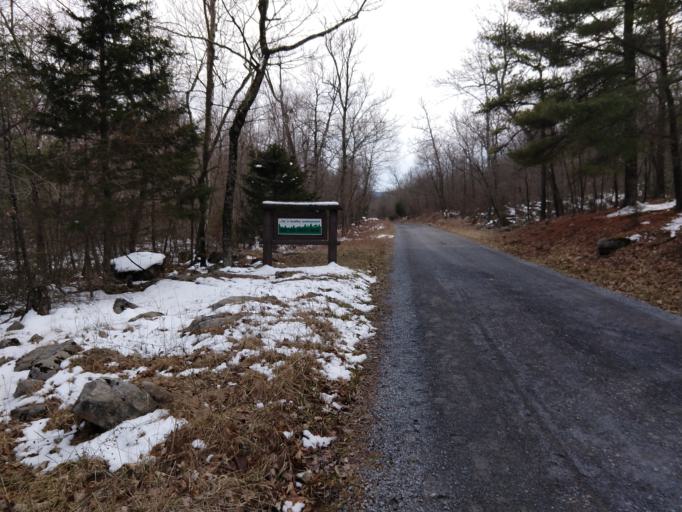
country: US
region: Virginia
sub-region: Shenandoah County
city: New Market
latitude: 38.6560
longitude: -78.6026
